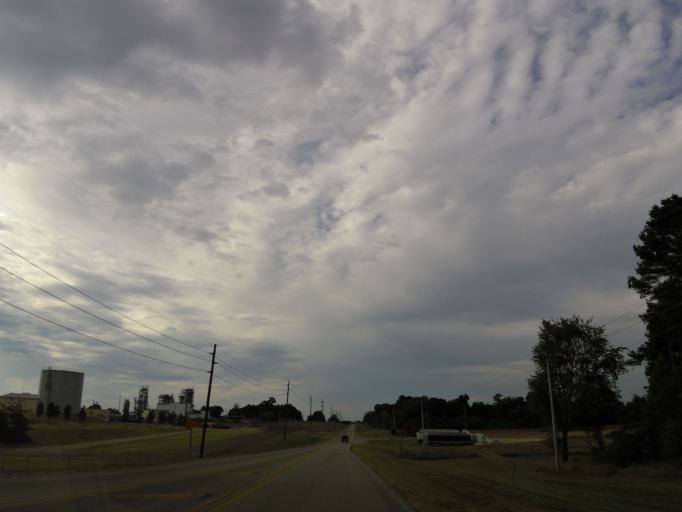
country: US
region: Alabama
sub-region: Morgan County
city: Trinity
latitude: 34.6317
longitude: -87.0384
